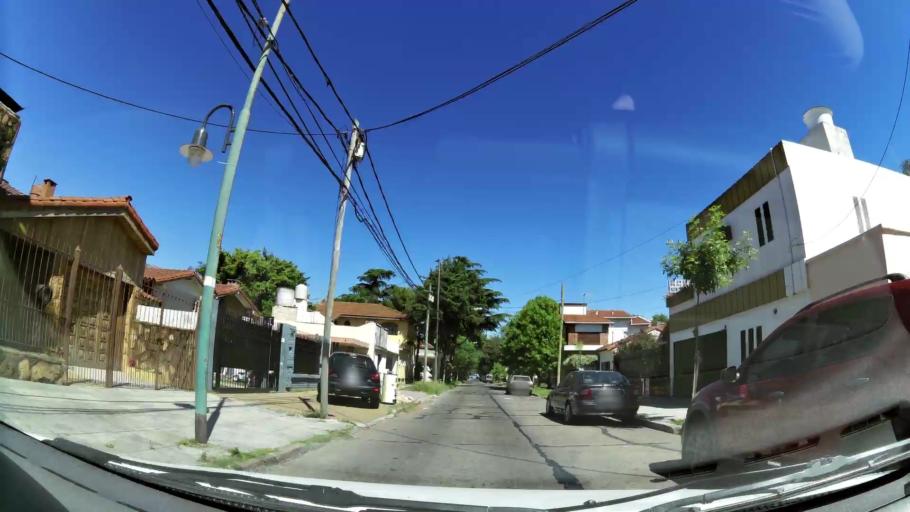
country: AR
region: Buenos Aires
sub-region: Partido de General San Martin
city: General San Martin
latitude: -34.5286
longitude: -58.5327
